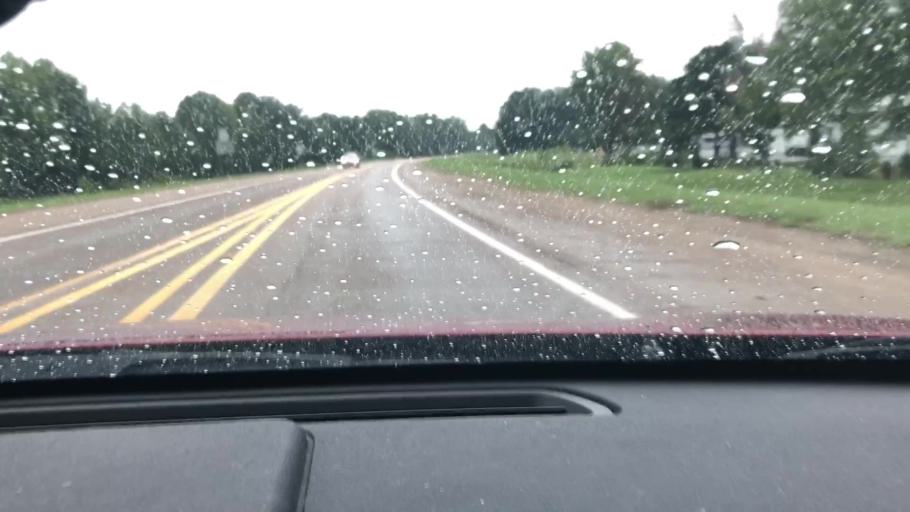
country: US
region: Arkansas
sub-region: Columbia County
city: Magnolia
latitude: 33.2963
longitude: -93.2527
